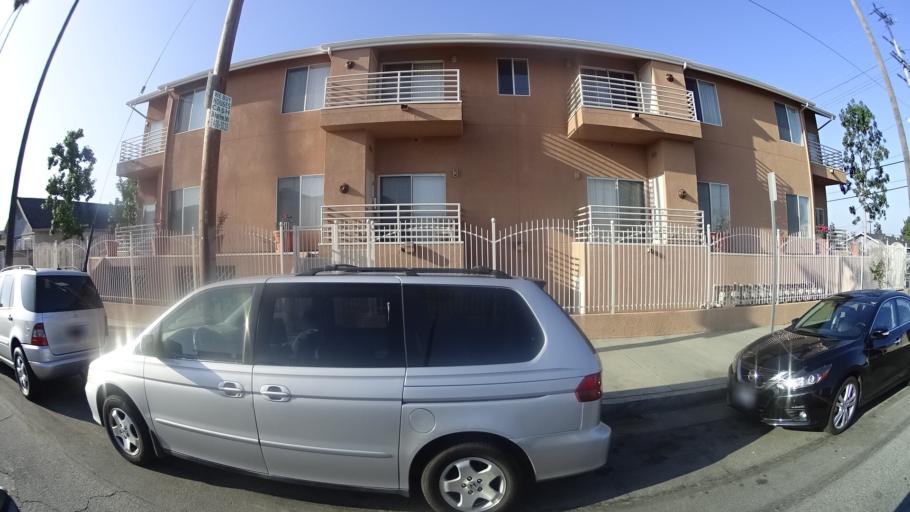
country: US
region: California
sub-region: Los Angeles County
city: Westmont
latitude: 33.9832
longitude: -118.2865
